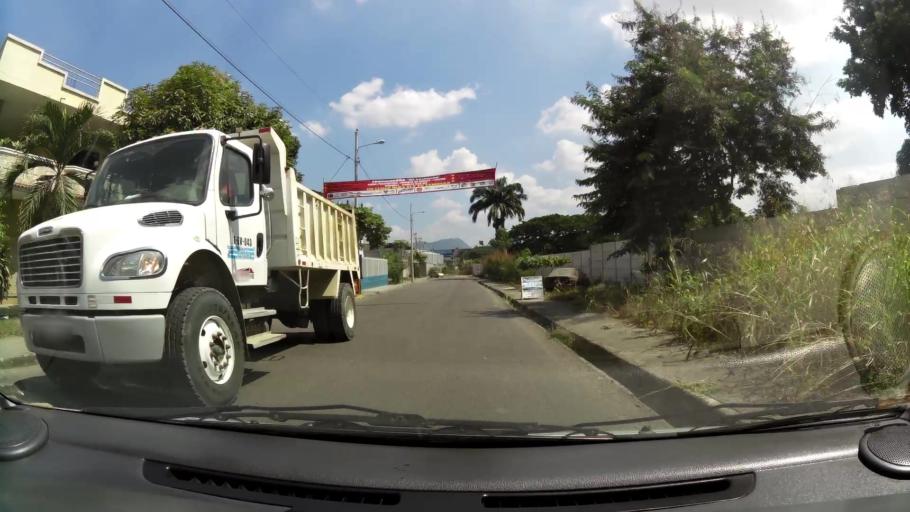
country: EC
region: Guayas
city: Guayaquil
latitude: -2.1190
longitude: -79.9279
